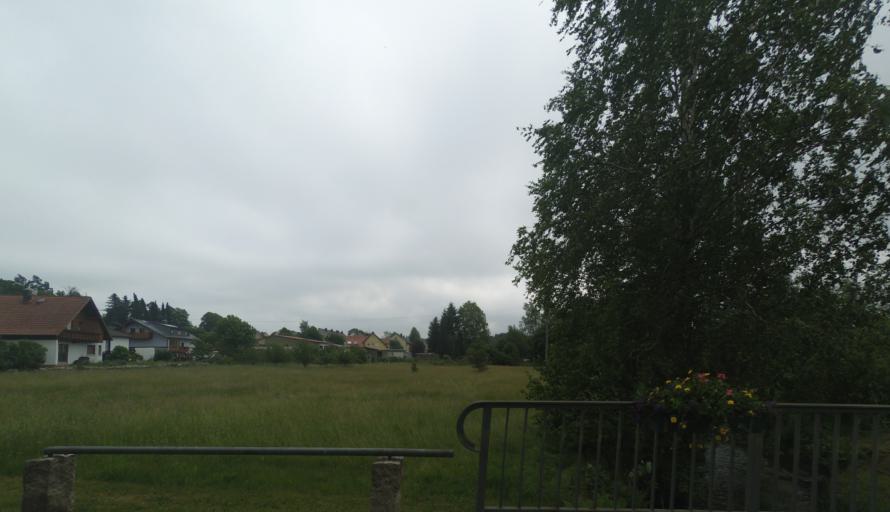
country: DE
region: Bavaria
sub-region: Upper Franconia
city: Roslau
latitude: 50.0878
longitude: 11.9610
